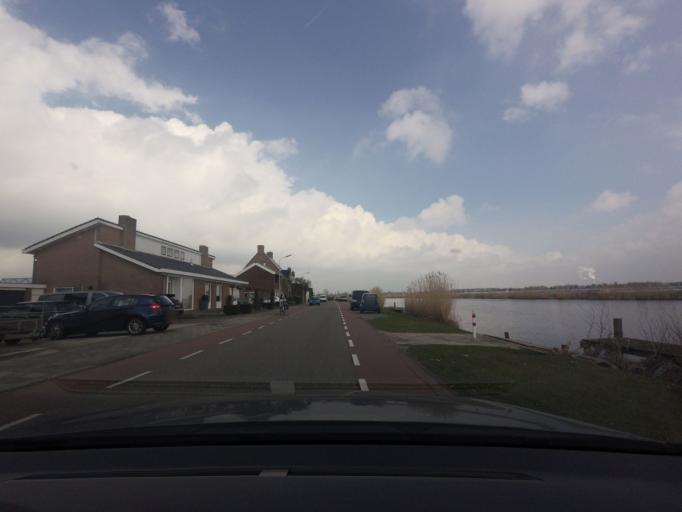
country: NL
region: North Holland
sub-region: Gemeente Zaanstad
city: Zaandam
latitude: 52.3730
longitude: 4.7582
